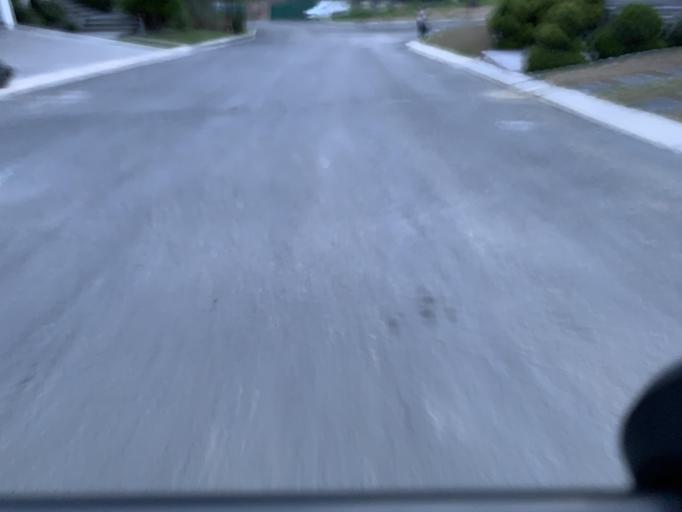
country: MX
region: Nuevo Leon
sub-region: Juarez
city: Bosques de San Pedro
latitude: 25.5127
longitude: -100.1841
